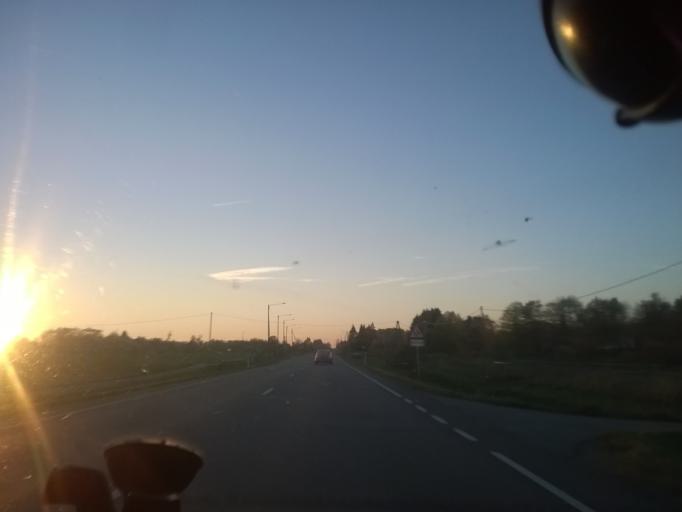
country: EE
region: Laeaene
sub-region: Ridala Parish
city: Uuemoisa
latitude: 58.9718
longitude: 23.8690
